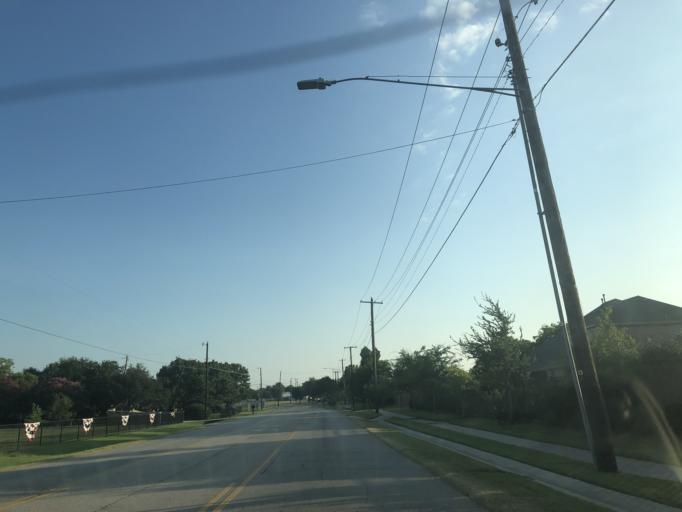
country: US
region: Texas
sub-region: Dallas County
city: Sunnyvale
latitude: 32.8451
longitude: -96.5605
